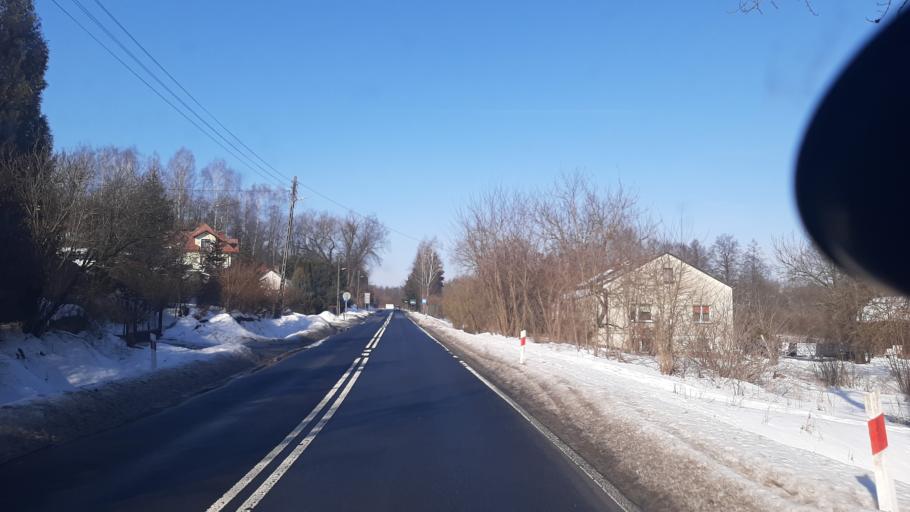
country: PL
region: Lublin Voivodeship
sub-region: Powiat pulawski
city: Wawolnica
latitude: 51.2877
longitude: 22.1641
